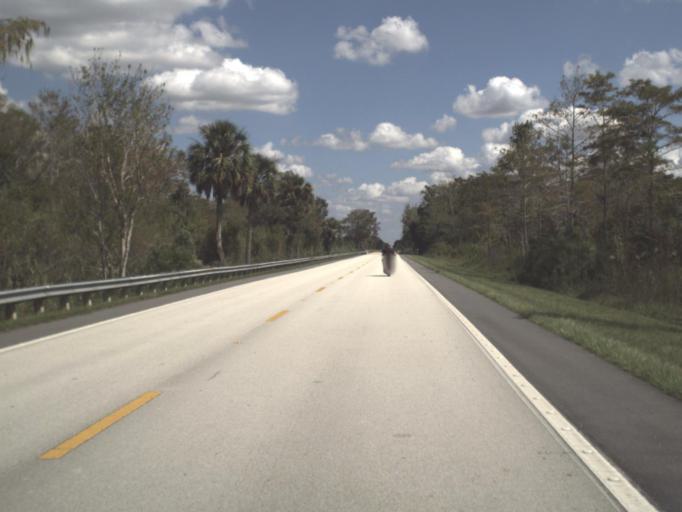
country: US
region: Florida
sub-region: Collier County
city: Marco
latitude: 25.8748
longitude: -81.2092
